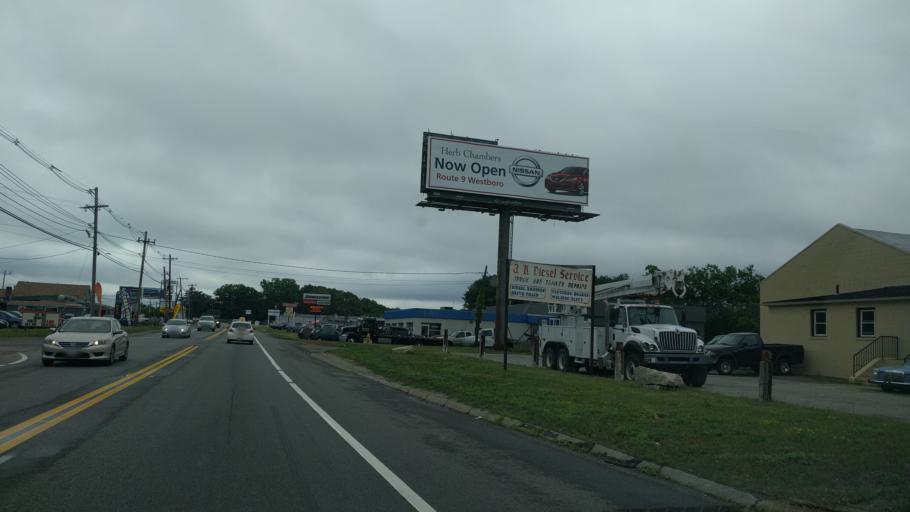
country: US
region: Massachusetts
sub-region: Worcester County
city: Sunderland
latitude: 42.2273
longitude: -71.7593
